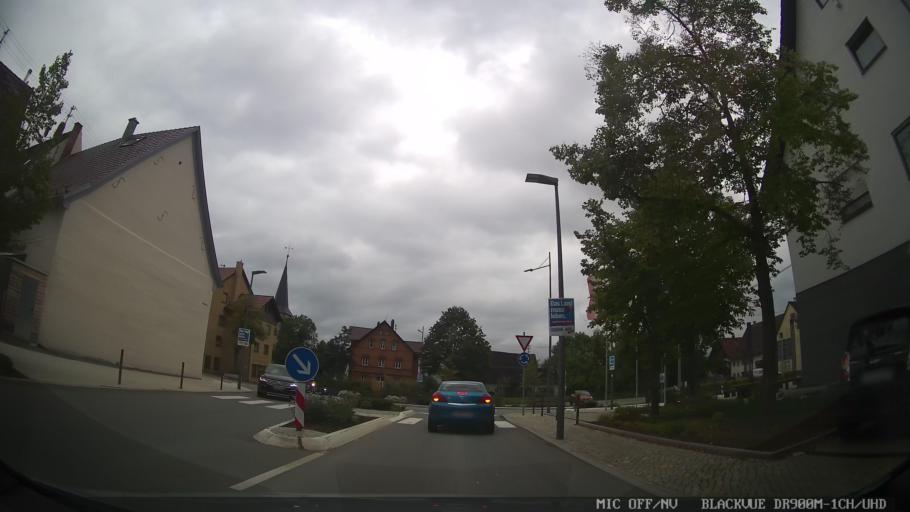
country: DE
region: Baden-Wuerttemberg
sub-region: Freiburg Region
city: Neuhausen ob Eck
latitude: 47.9740
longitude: 8.9261
